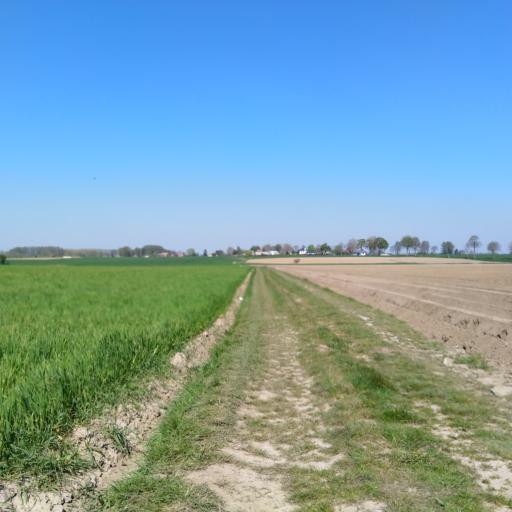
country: BE
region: Wallonia
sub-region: Province du Hainaut
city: Jurbise
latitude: 50.5395
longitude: 3.9035
